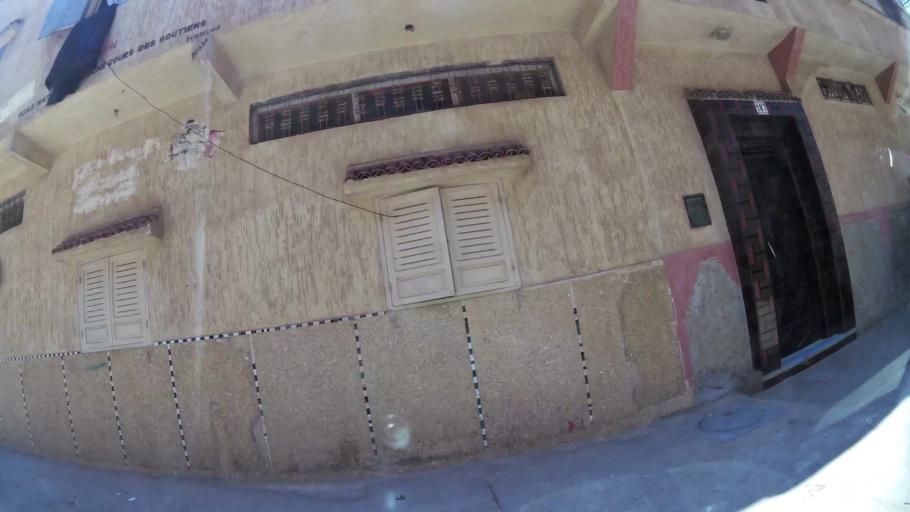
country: MA
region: Rabat-Sale-Zemmour-Zaer
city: Sale
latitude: 34.0680
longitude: -6.7885
